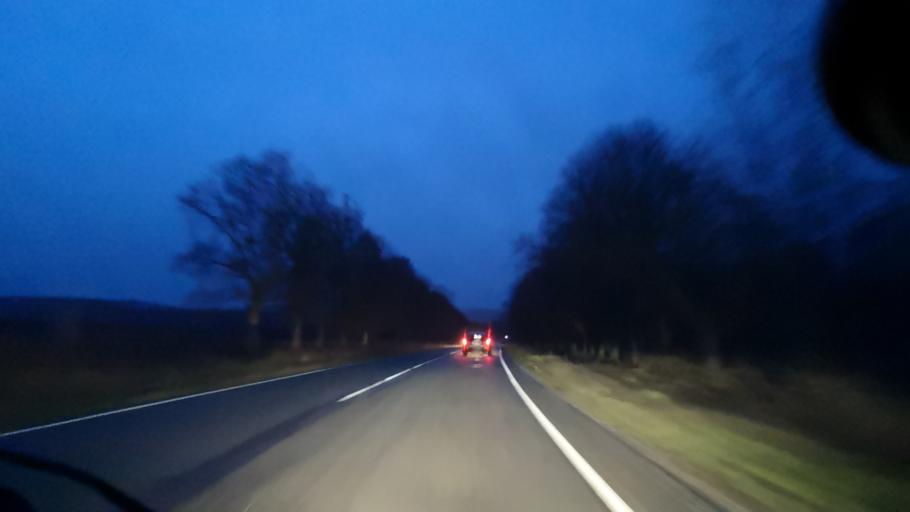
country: MD
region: Orhei
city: Orhei
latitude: 47.4806
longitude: 28.7910
